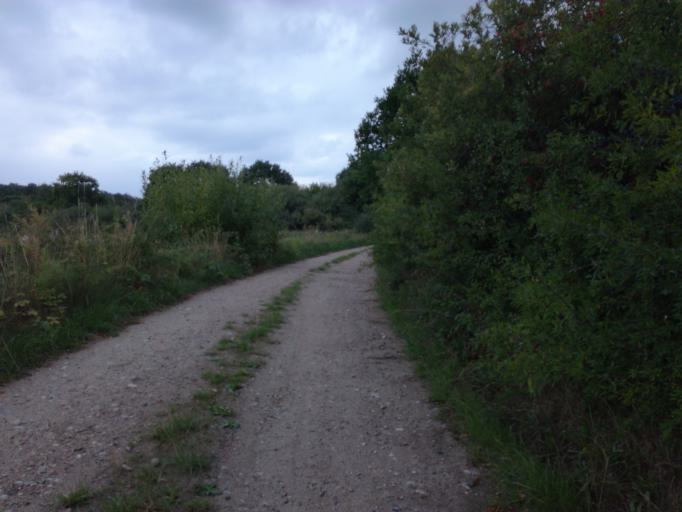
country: DK
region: South Denmark
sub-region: Fredericia Kommune
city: Fredericia
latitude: 55.6042
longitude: 9.7848
